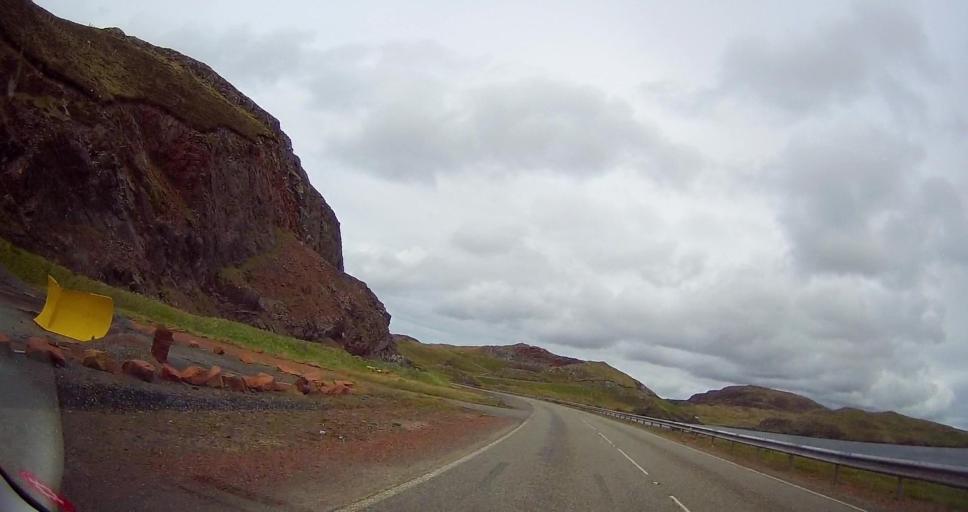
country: GB
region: Scotland
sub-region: Shetland Islands
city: Lerwick
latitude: 60.3946
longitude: -1.3784
